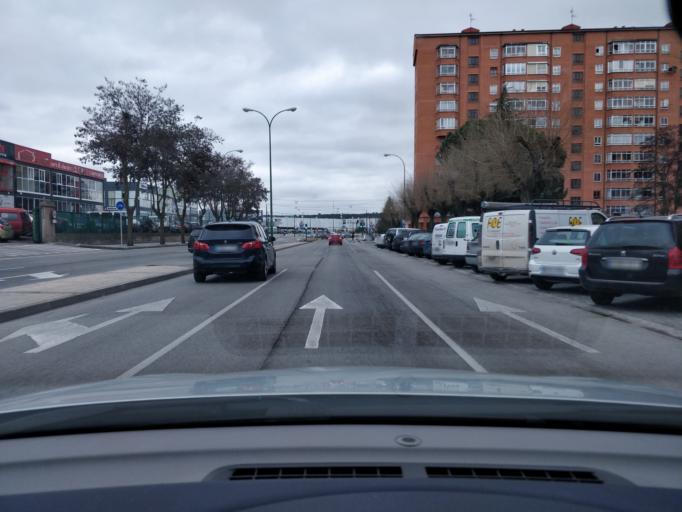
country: ES
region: Castille and Leon
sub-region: Provincia de Burgos
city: Burgos
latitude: 42.3519
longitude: -3.6614
